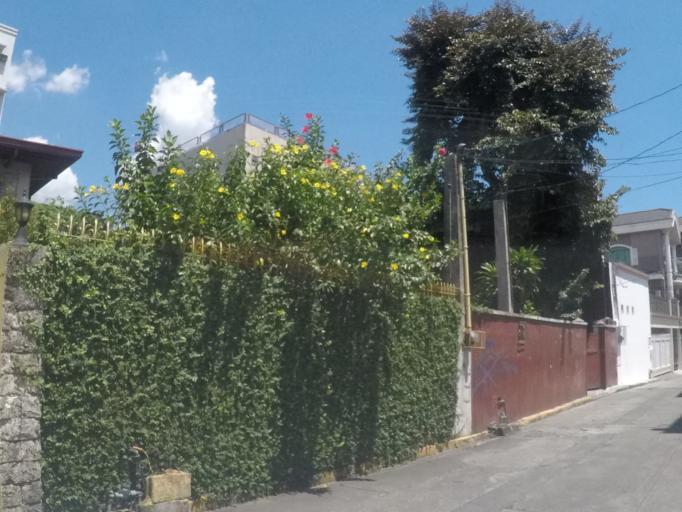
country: PH
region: Metro Manila
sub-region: San Juan
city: San Juan
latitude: 14.5997
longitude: 121.0273
